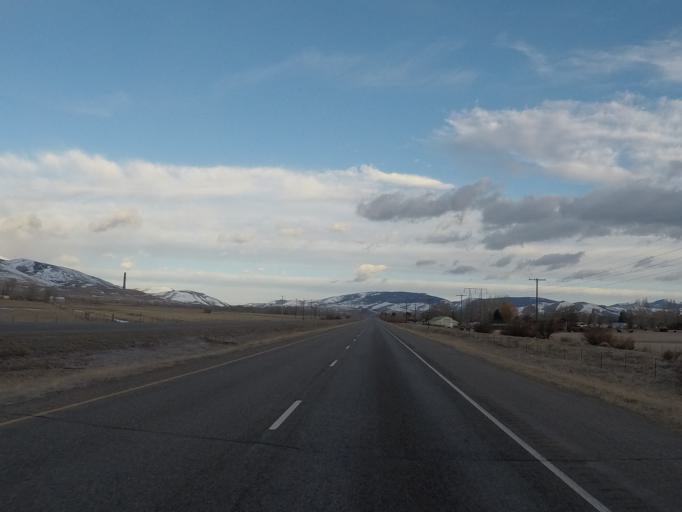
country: US
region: Montana
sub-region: Deer Lodge County
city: Warm Springs
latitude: 46.0997
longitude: -112.8327
